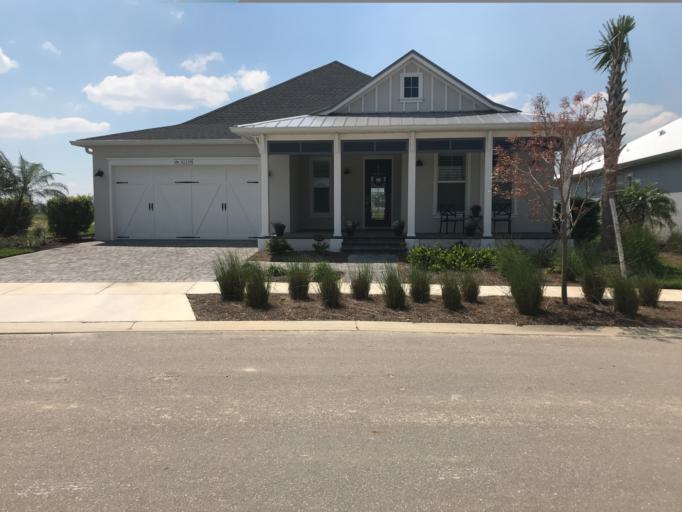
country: US
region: Florida
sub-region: Lee County
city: Fort Myers Shores
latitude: 26.7867
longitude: -81.7502
